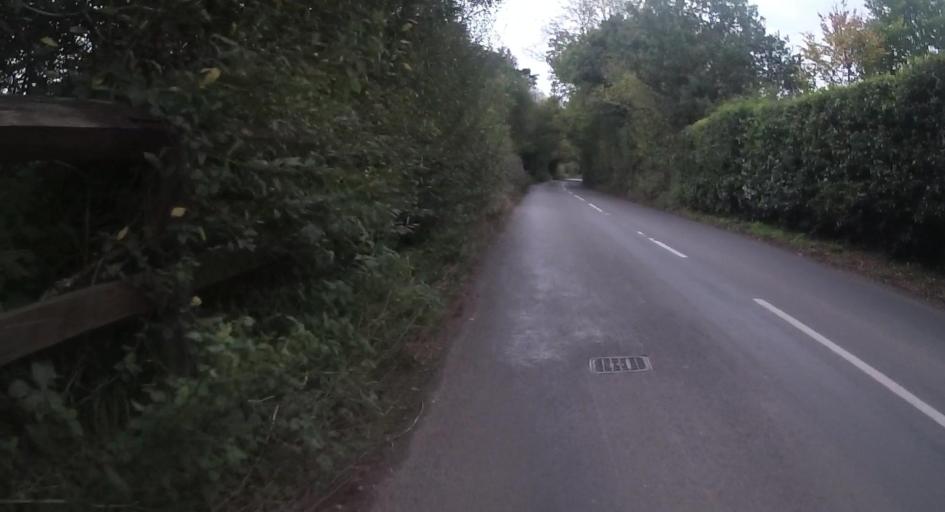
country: GB
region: England
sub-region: Hampshire
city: Fleet
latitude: 51.2481
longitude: -0.8612
